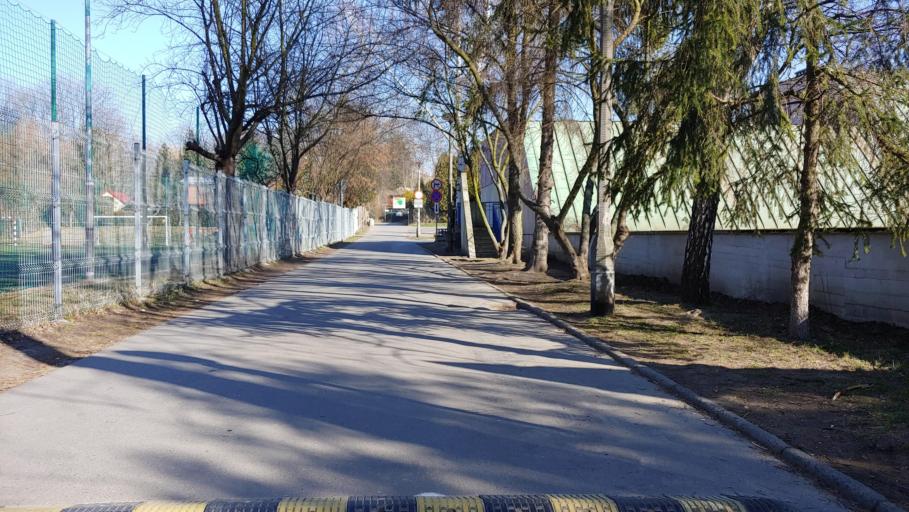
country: PL
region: Lesser Poland Voivodeship
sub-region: Krakow
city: Krakow
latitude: 50.0839
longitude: 19.9218
